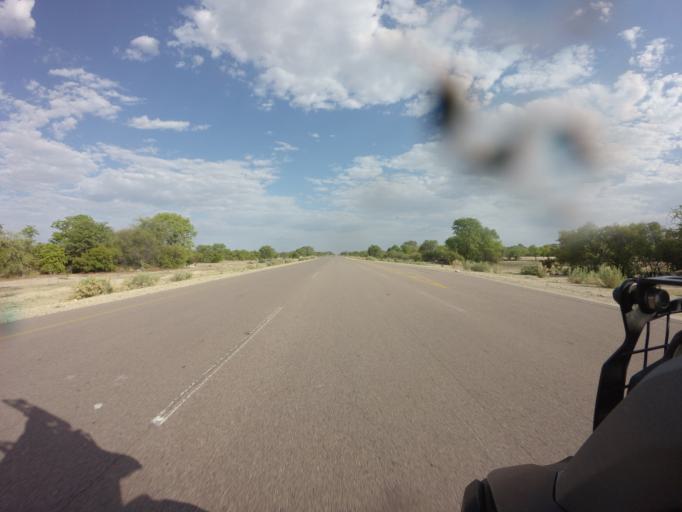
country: AO
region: Cunene
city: Ondjiva
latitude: -16.9917
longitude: 15.6280
